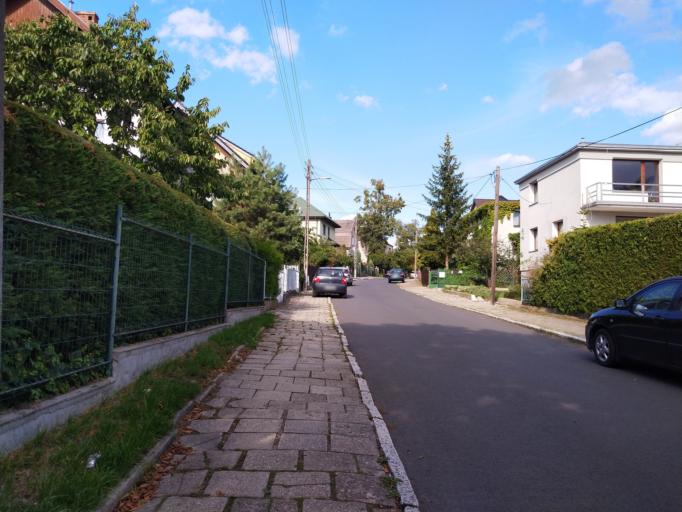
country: PL
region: West Pomeranian Voivodeship
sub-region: Szczecin
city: Szczecin
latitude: 53.4621
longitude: 14.5712
